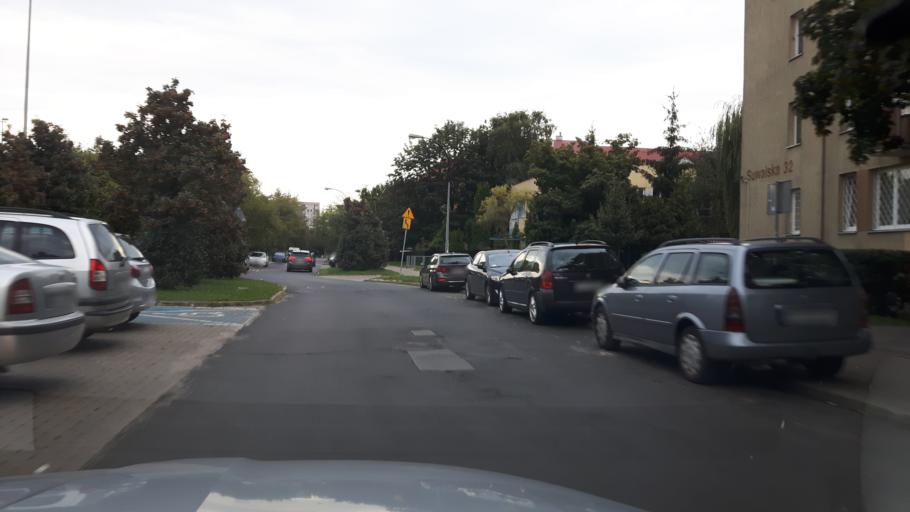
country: PL
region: Masovian Voivodeship
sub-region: Warszawa
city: Targowek
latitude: 52.2948
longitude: 21.0378
